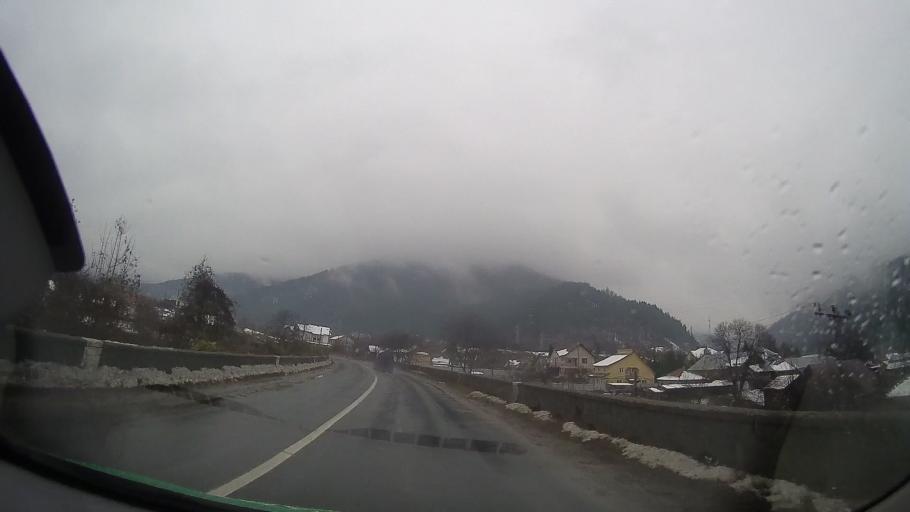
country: RO
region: Neamt
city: Viisoara
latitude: 46.9309
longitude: 26.2206
